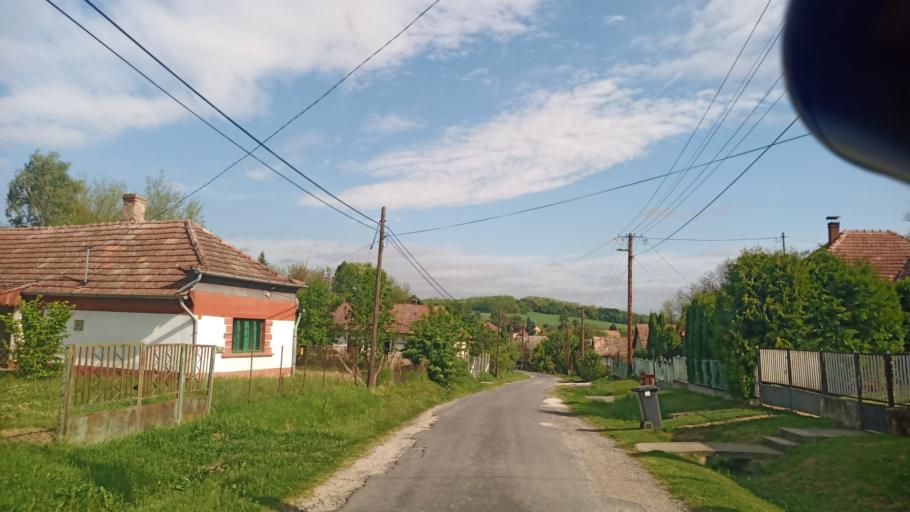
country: HU
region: Zala
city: Pacsa
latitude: 46.6690
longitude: 17.0793
